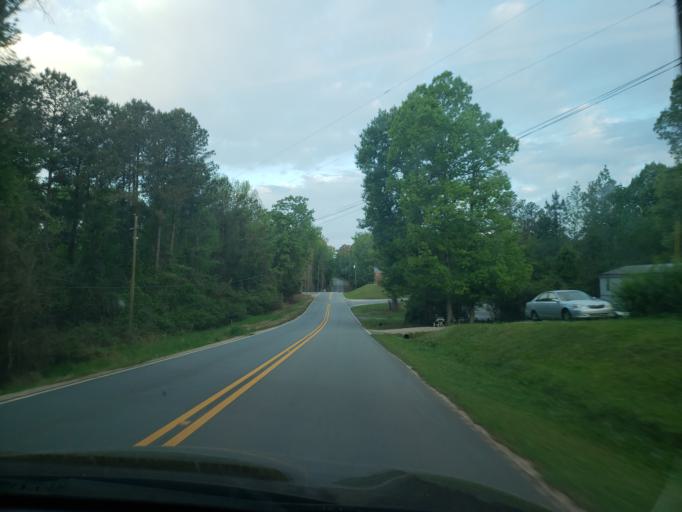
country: US
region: Alabama
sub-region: Tallapoosa County
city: Dadeville
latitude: 32.7018
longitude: -85.7468
